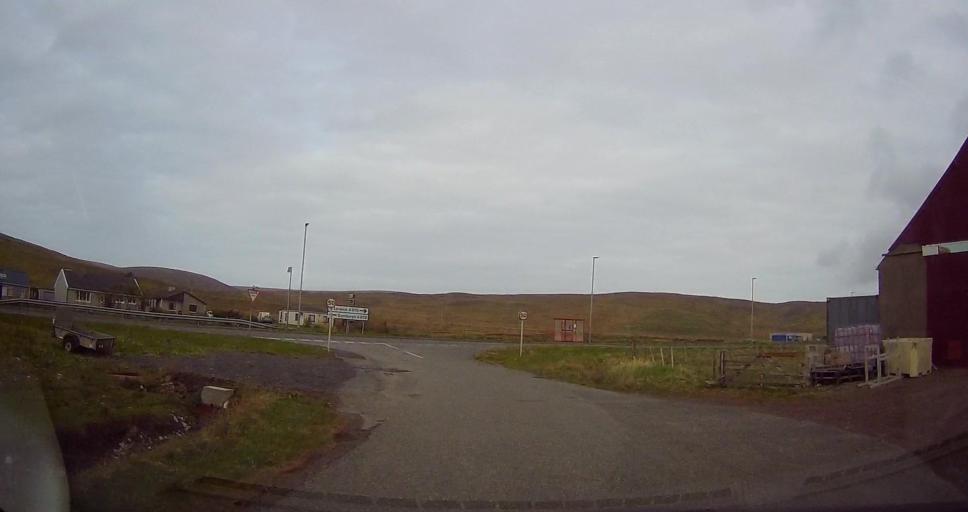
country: GB
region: Scotland
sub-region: Shetland Islands
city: Sandwick
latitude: 60.0556
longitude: -1.2247
